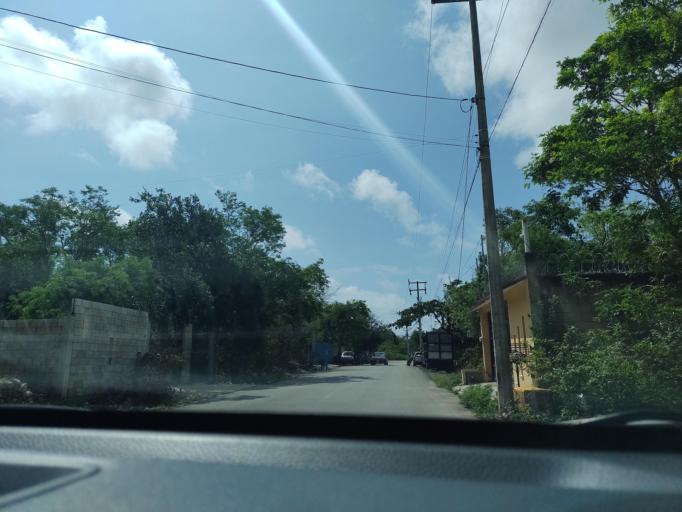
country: MX
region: Quintana Roo
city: Tulum
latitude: 20.2127
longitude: -87.4723
